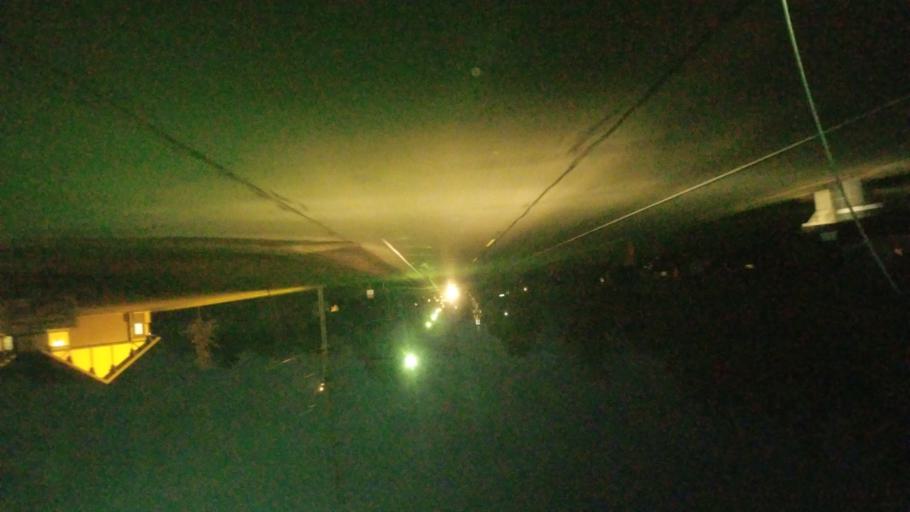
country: US
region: Indiana
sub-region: Adams County
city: Berne
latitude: 40.6573
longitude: -84.9645
